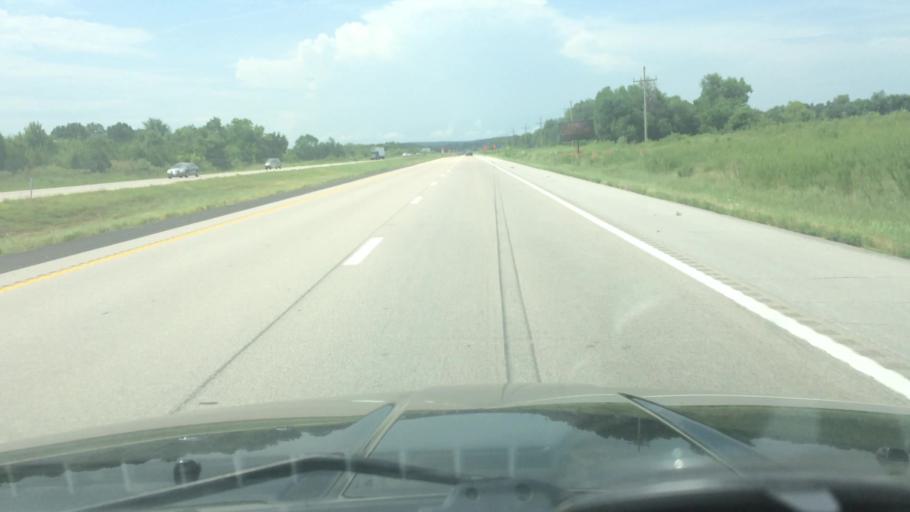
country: US
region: Missouri
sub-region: Polk County
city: Humansville
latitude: 37.8072
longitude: -93.6013
